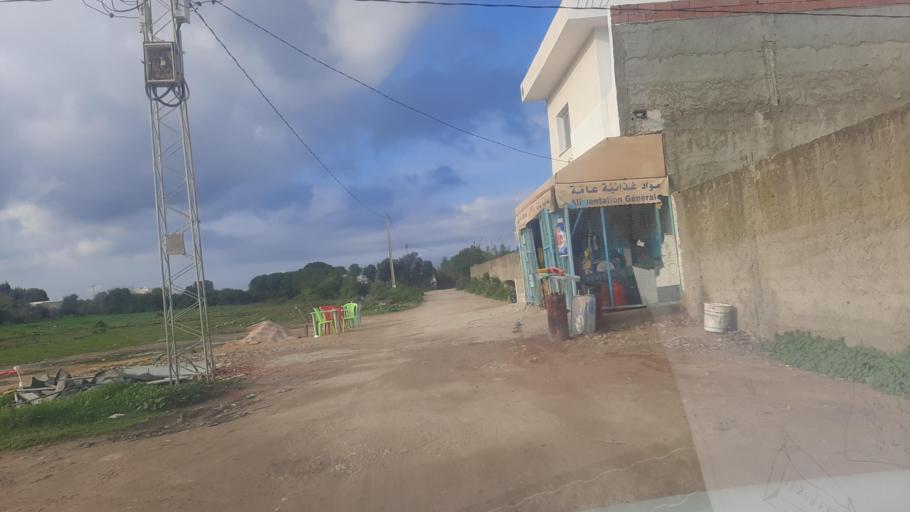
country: TN
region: Nabul
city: Manzil Bu Zalafah
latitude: 36.7166
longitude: 10.4965
